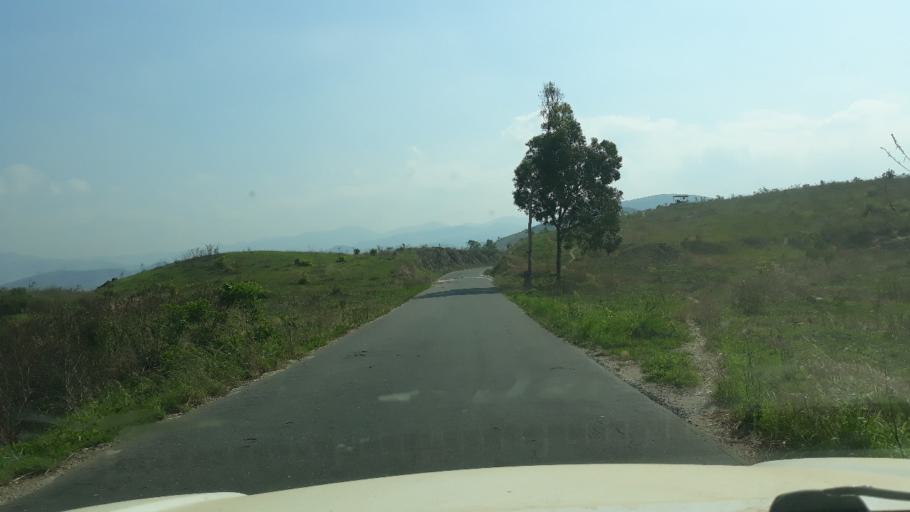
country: CD
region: South Kivu
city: Uvira
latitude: -3.2010
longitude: 29.1580
